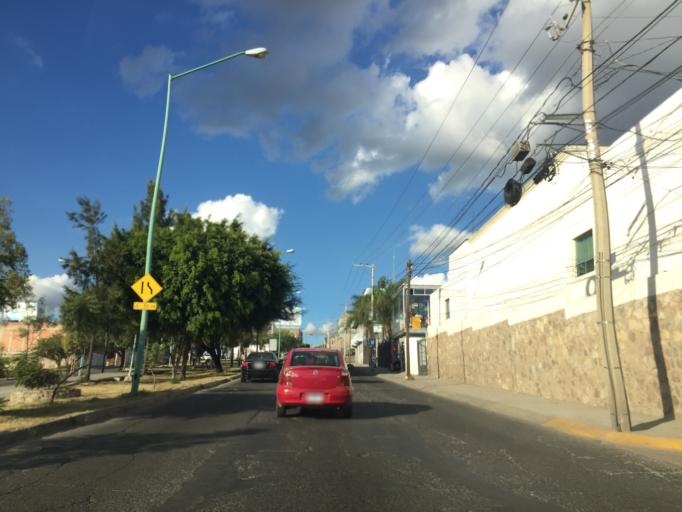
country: MX
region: Guanajuato
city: Leon
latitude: 21.1229
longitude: -101.7064
